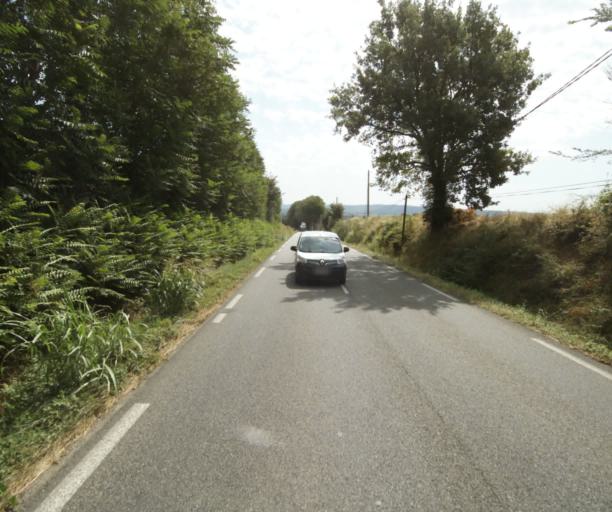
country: FR
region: Midi-Pyrenees
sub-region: Departement de la Haute-Garonne
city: Saint-Felix-Lauragais
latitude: 43.4496
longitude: 1.9084
